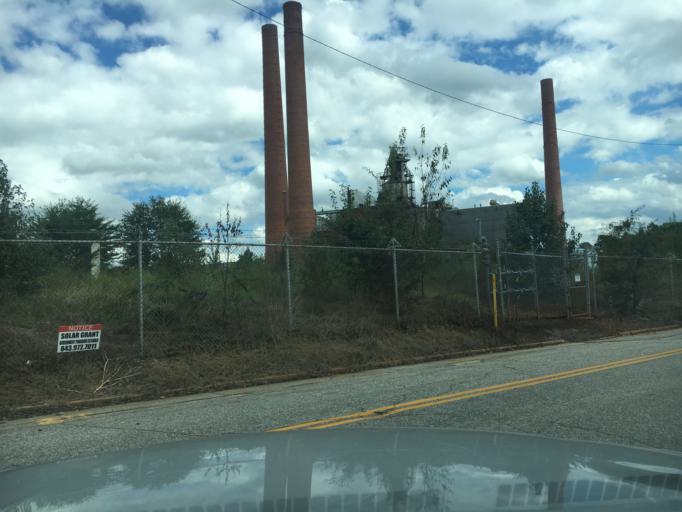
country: US
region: South Carolina
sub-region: Spartanburg County
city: Lyman
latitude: 34.9443
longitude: -82.1275
